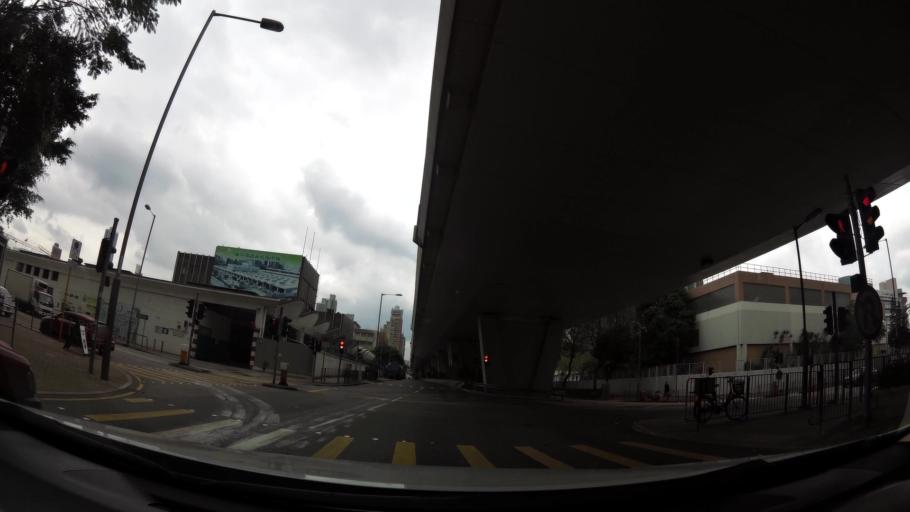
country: HK
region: Sham Shui Po
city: Sham Shui Po
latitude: 22.3327
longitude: 114.1523
